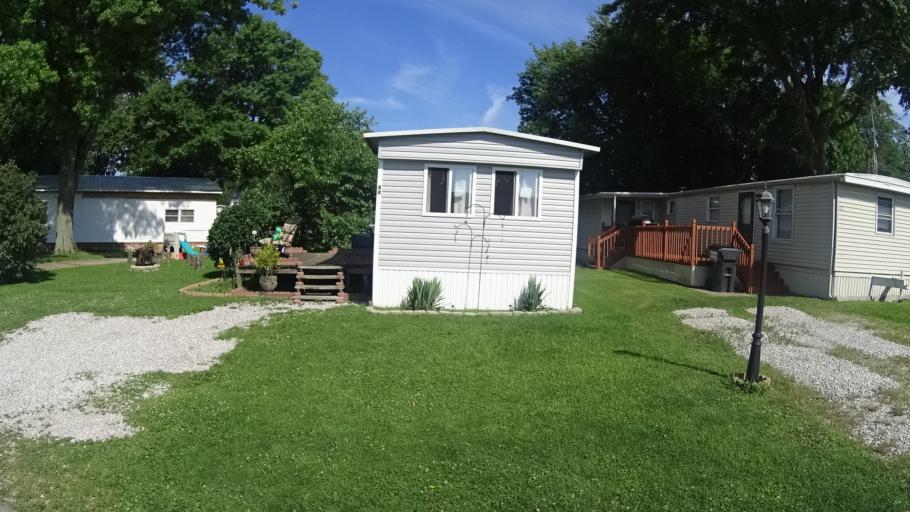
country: US
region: Ohio
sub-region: Erie County
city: Huron
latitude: 41.3812
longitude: -82.4670
